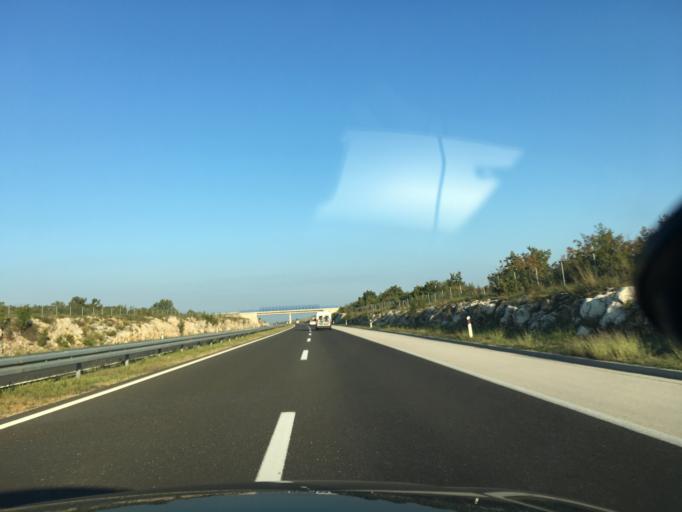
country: HR
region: Zadarska
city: Polaca
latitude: 44.0862
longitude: 15.5002
